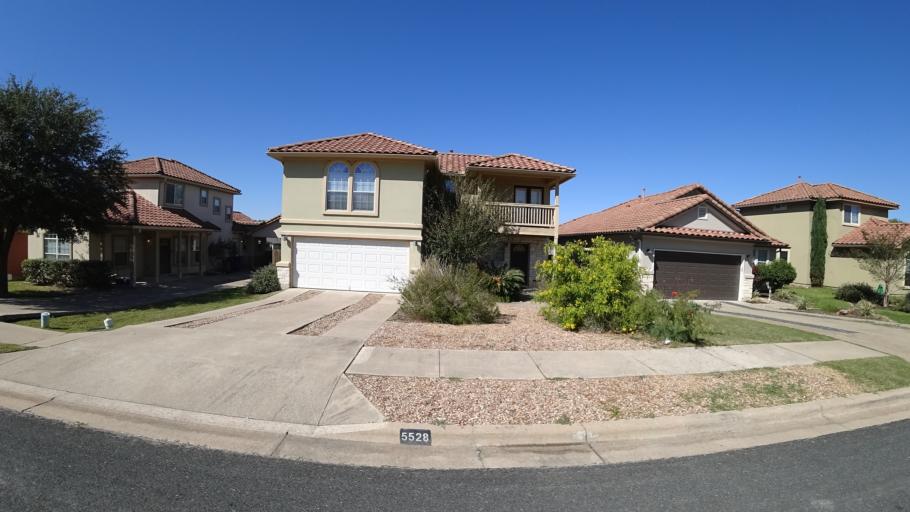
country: US
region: Texas
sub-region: Travis County
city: Hornsby Bend
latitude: 30.2870
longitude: -97.6460
